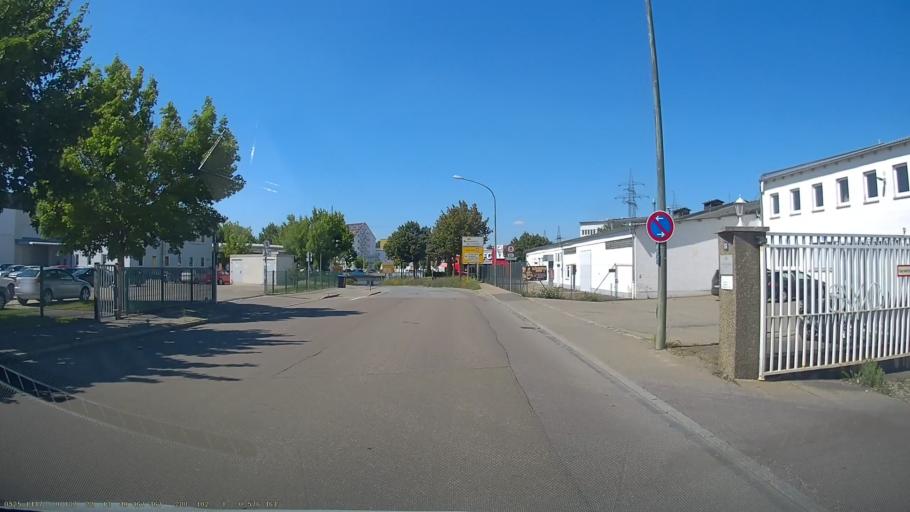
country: DE
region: Bavaria
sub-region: Swabia
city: Neu-Ulm
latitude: 48.3945
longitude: 10.0219
